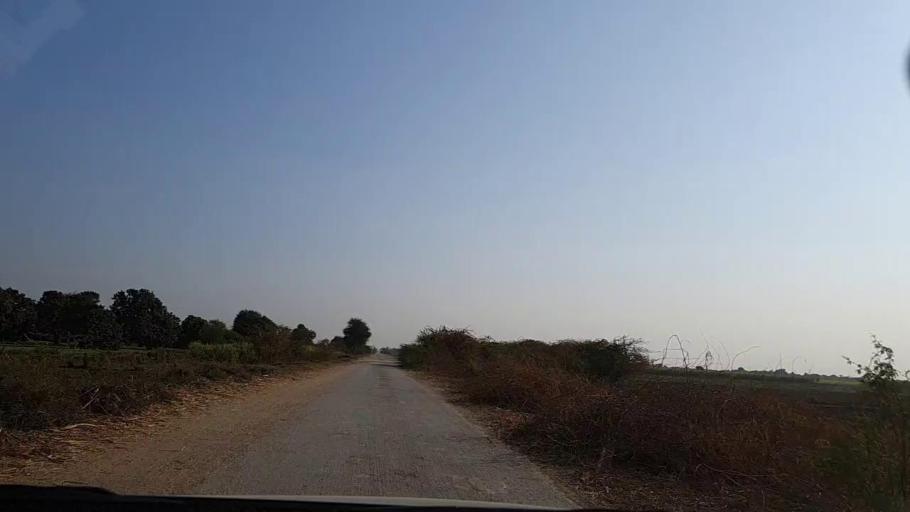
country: PK
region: Sindh
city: Tando Ghulam Ali
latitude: 25.2197
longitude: 68.9460
